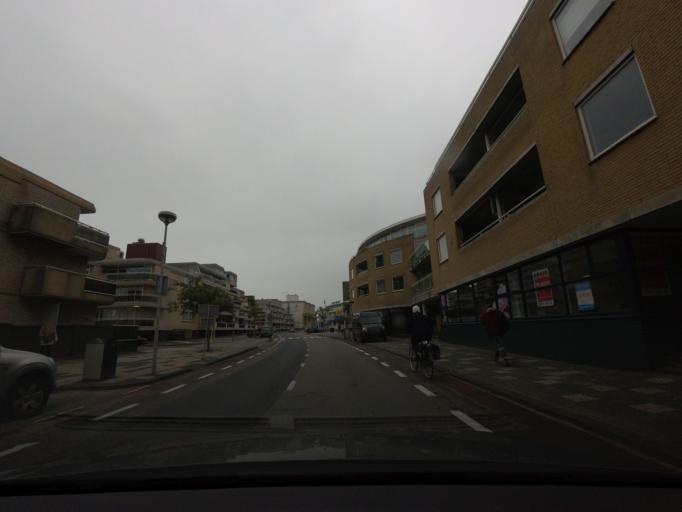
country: NL
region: South Holland
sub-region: Gemeente Noordwijk
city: Noordwijk-Binnen
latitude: 52.2451
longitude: 4.4320
